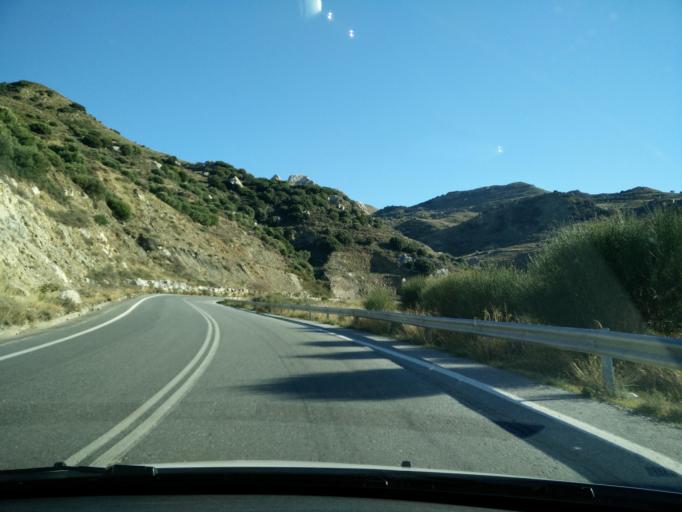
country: GR
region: Crete
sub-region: Nomos Irakleiou
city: Arkalochori
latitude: 35.0708
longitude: 25.3599
